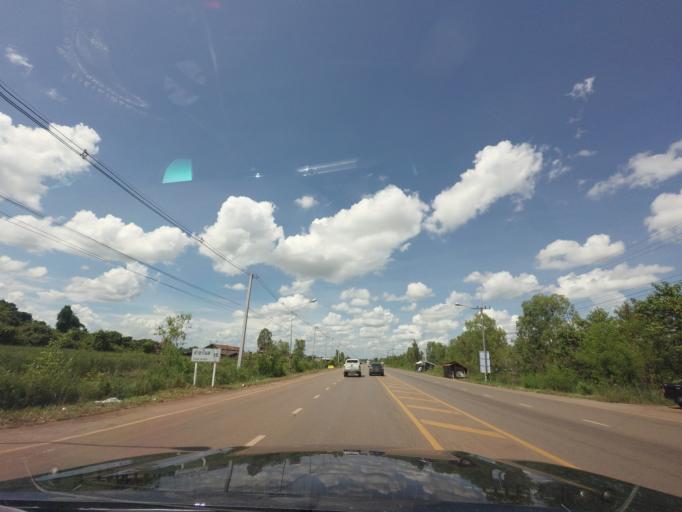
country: TH
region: Changwat Udon Thani
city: Ban Dung
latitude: 17.7146
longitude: 103.2502
